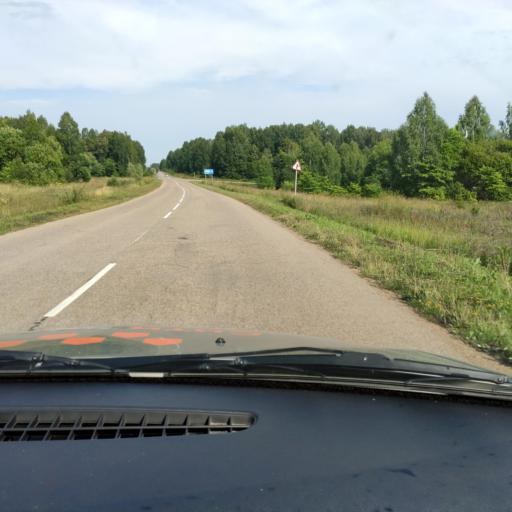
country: RU
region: Bashkortostan
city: Pavlovka
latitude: 55.3859
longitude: 56.5041
